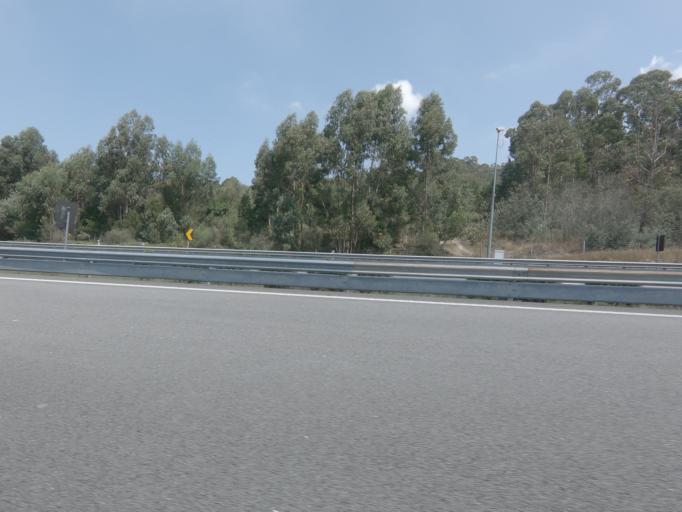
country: PT
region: Porto
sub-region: Valongo
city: Campo
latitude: 41.1957
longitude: -8.4863
